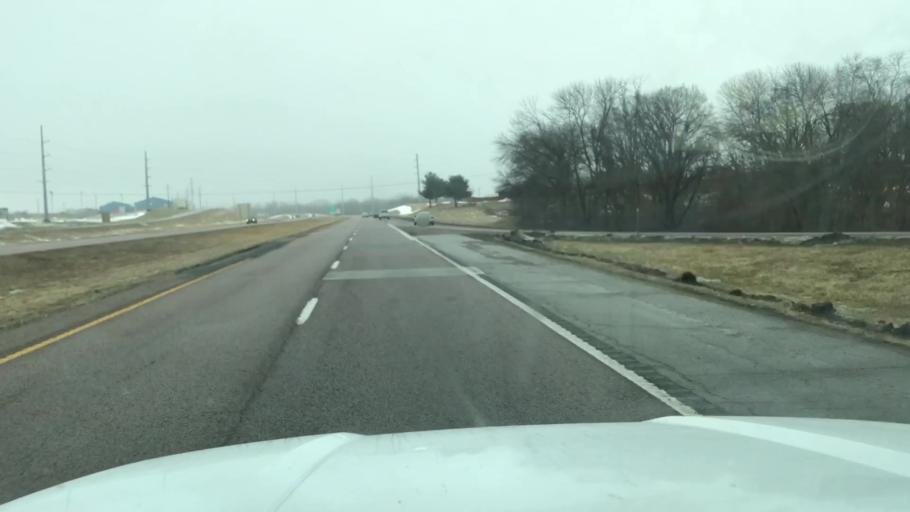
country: US
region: Missouri
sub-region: Buchanan County
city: Saint Joseph
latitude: 39.7503
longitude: -94.7704
